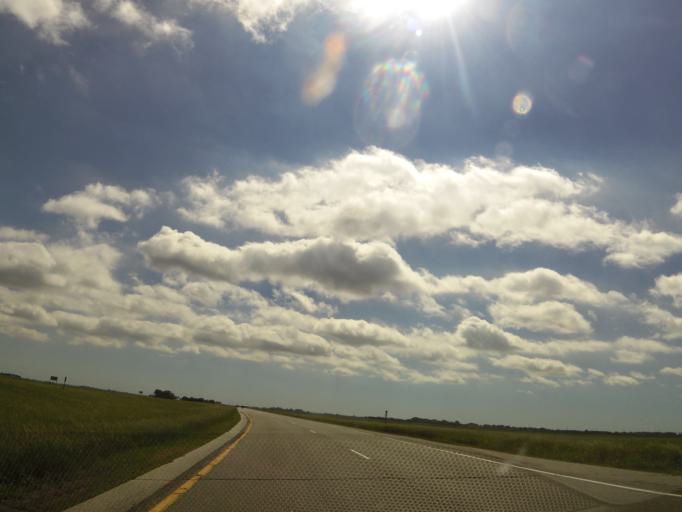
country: US
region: Minnesota
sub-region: Polk County
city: Crookston
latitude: 47.8036
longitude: -96.7942
